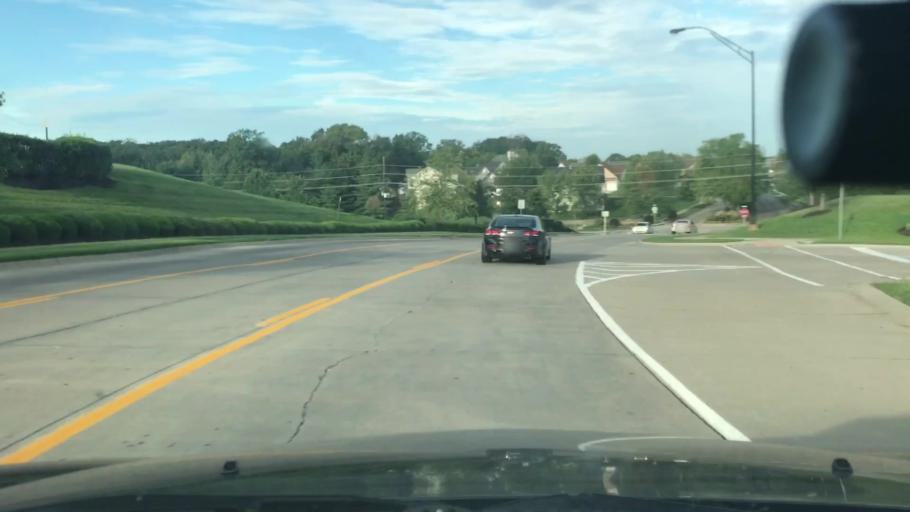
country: US
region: Missouri
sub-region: Saint Charles County
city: Wentzville
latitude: 38.8126
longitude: -90.8815
